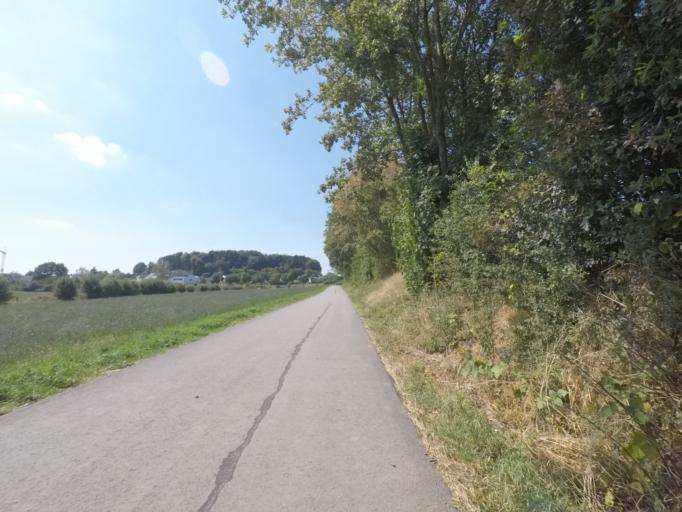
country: LU
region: Luxembourg
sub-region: Canton de Capellen
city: Garnich
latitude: 49.6222
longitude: 5.9545
